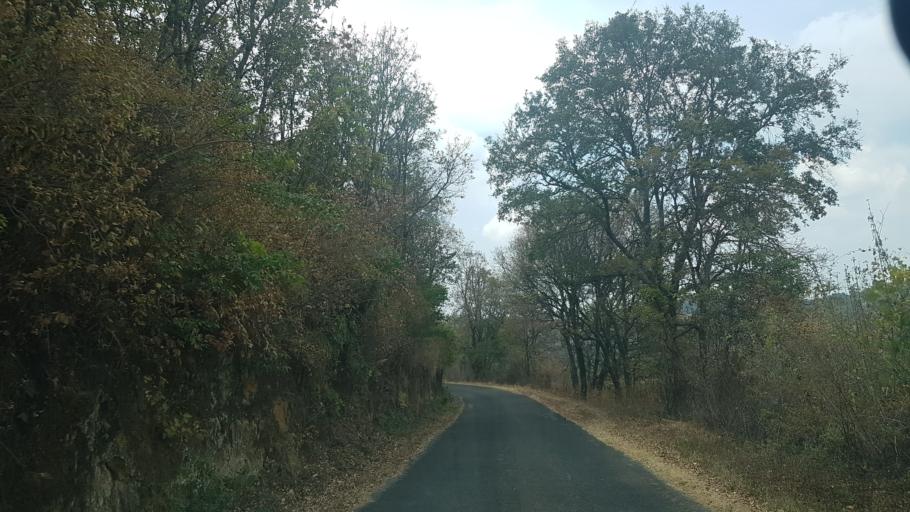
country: MX
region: Puebla
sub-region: Atzitzihuacan
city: Santiago Atzitzihuacan
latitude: 18.8398
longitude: -98.6143
